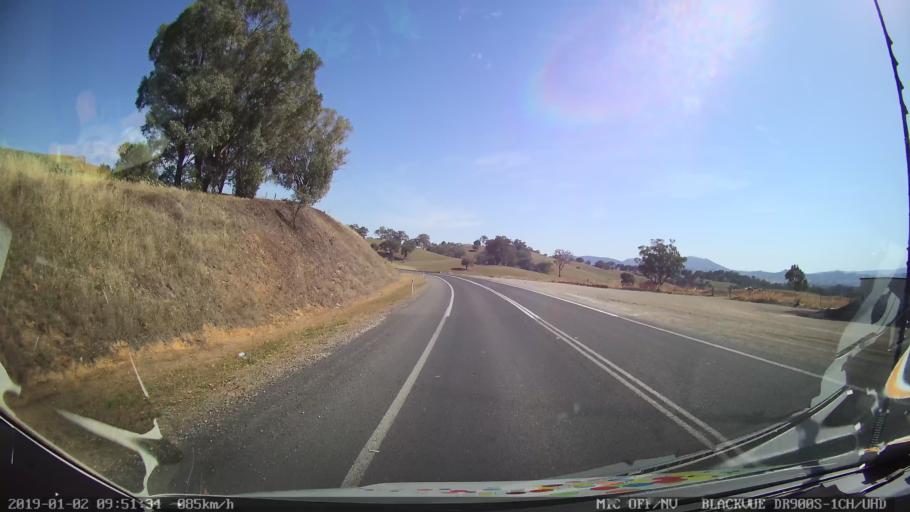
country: AU
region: New South Wales
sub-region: Tumut Shire
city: Tumut
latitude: -35.2716
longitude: 148.2114
